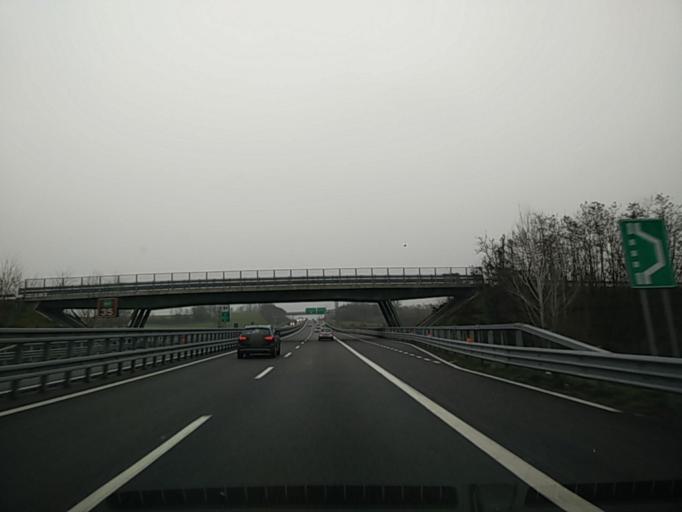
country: IT
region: Piedmont
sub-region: Provincia di Alessandria
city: Quattordio
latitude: 44.9078
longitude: 8.3987
